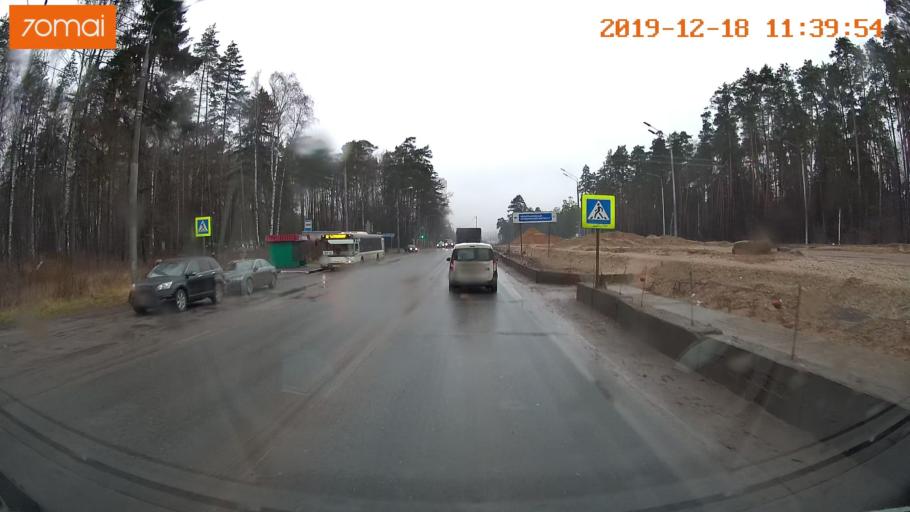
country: RU
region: Moskovskaya
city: Zvenigorod
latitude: 55.7037
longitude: 36.8791
